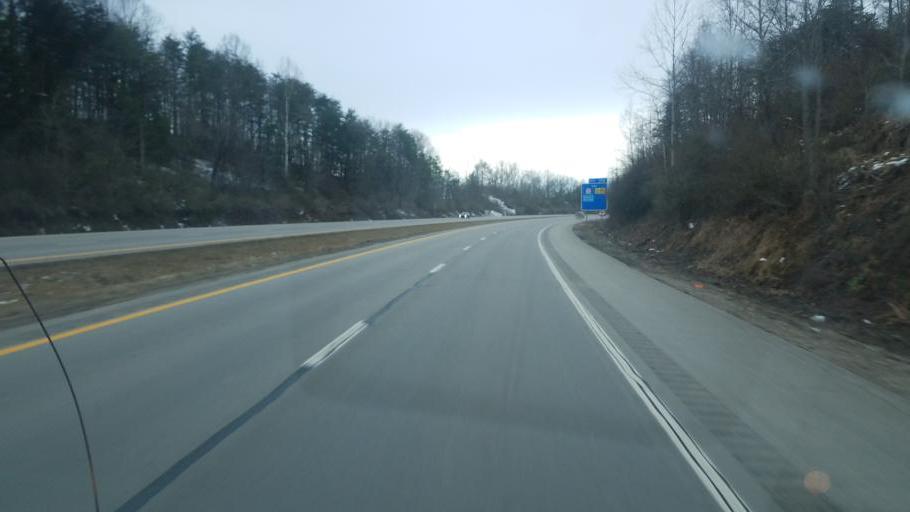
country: US
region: West Virginia
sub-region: Wood County
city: Mineral Wells
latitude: 39.2067
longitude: -81.5202
